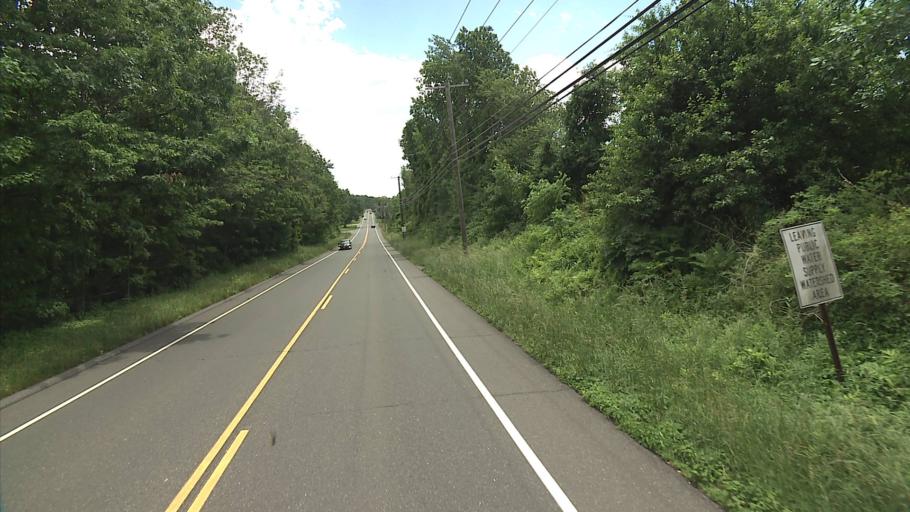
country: US
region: Connecticut
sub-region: Litchfield County
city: Watertown
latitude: 41.6351
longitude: -73.1411
